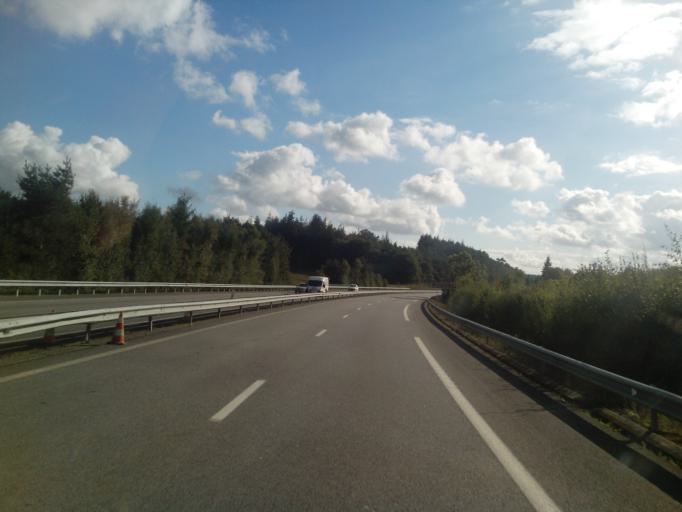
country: FR
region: Brittany
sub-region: Departement du Morbihan
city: Malestroit
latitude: 47.8048
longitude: -2.4440
